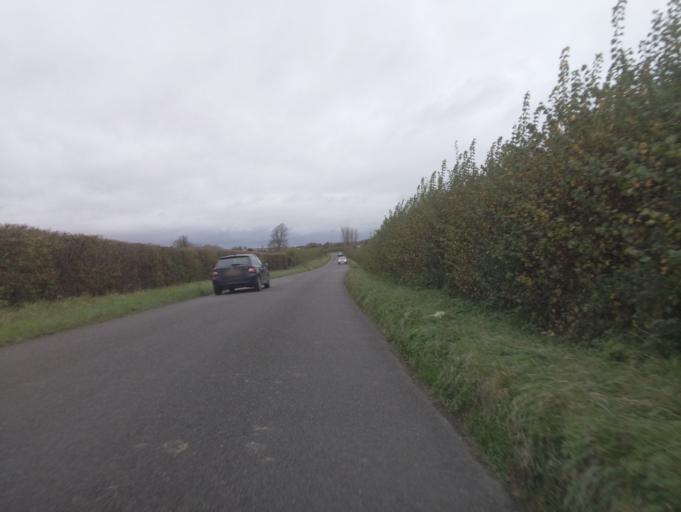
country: GB
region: England
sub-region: Somerset
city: Yeovil
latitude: 51.0129
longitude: -2.5995
